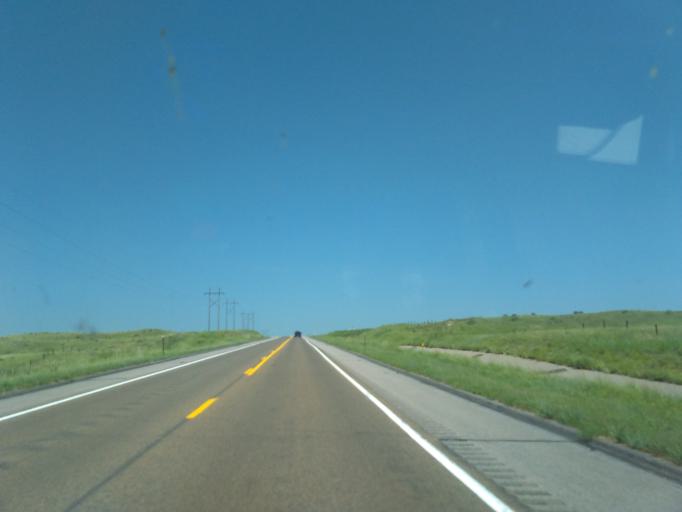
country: US
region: Nebraska
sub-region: Lincoln County
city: North Platte
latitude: 40.8704
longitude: -100.7540
